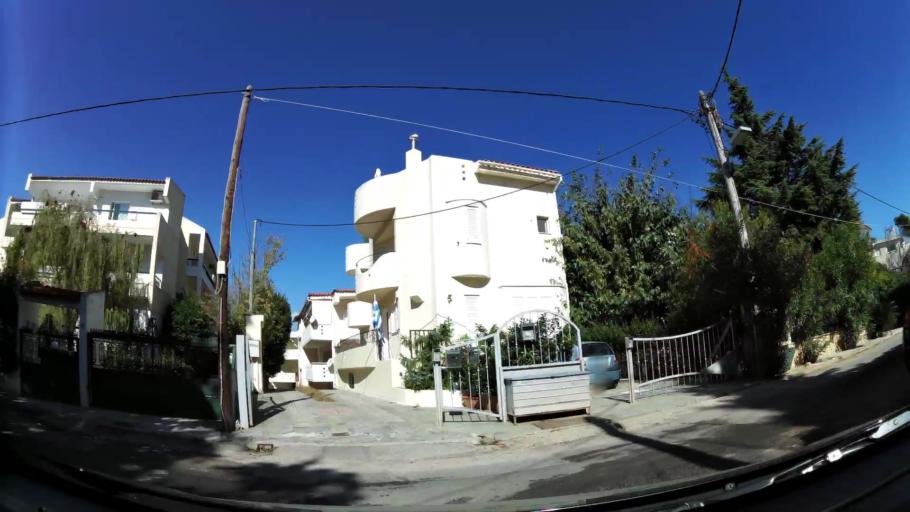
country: GR
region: Attica
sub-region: Nomarchia Anatolikis Attikis
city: Drosia
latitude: 38.1209
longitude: 23.8656
